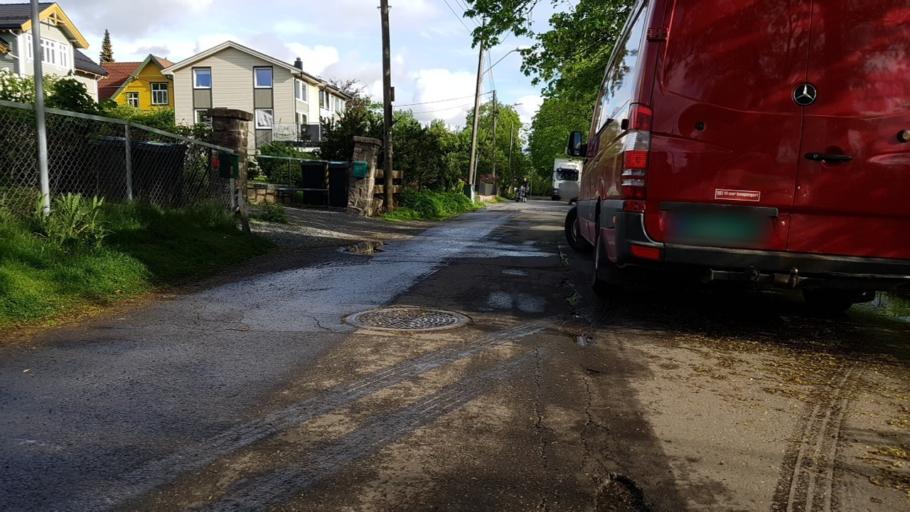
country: NO
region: Oslo
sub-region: Oslo
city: Oslo
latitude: 59.9427
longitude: 10.7885
